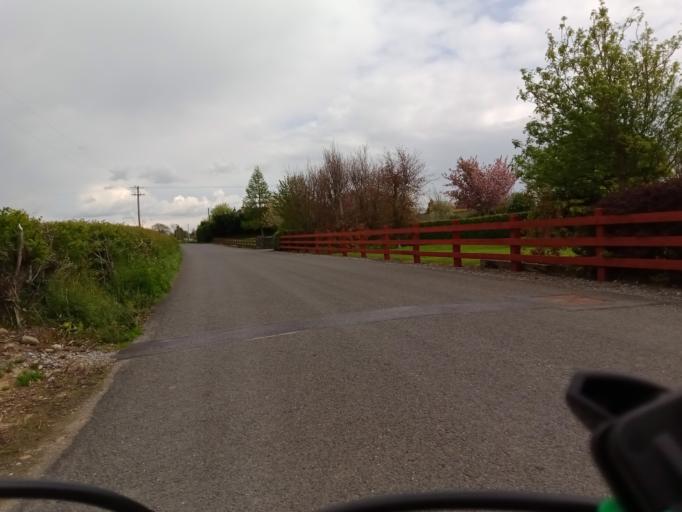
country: IE
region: Leinster
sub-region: Kilkenny
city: Kilkenny
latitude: 52.5994
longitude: -7.2644
